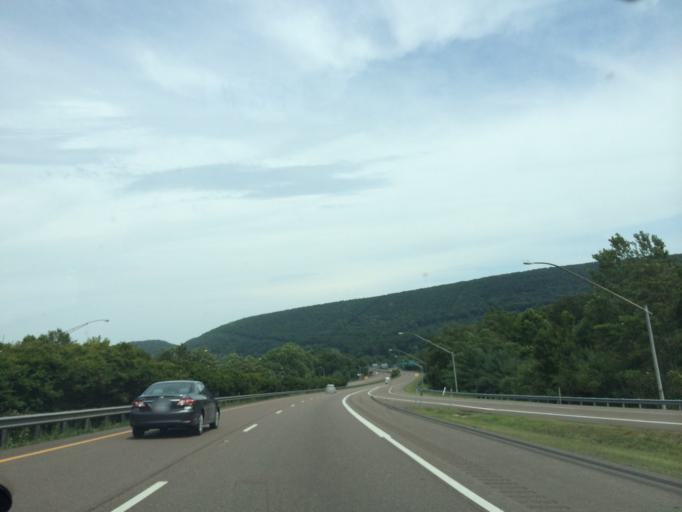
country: US
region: Maryland
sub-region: Allegany County
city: La Vale
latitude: 39.6353
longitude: -78.8404
